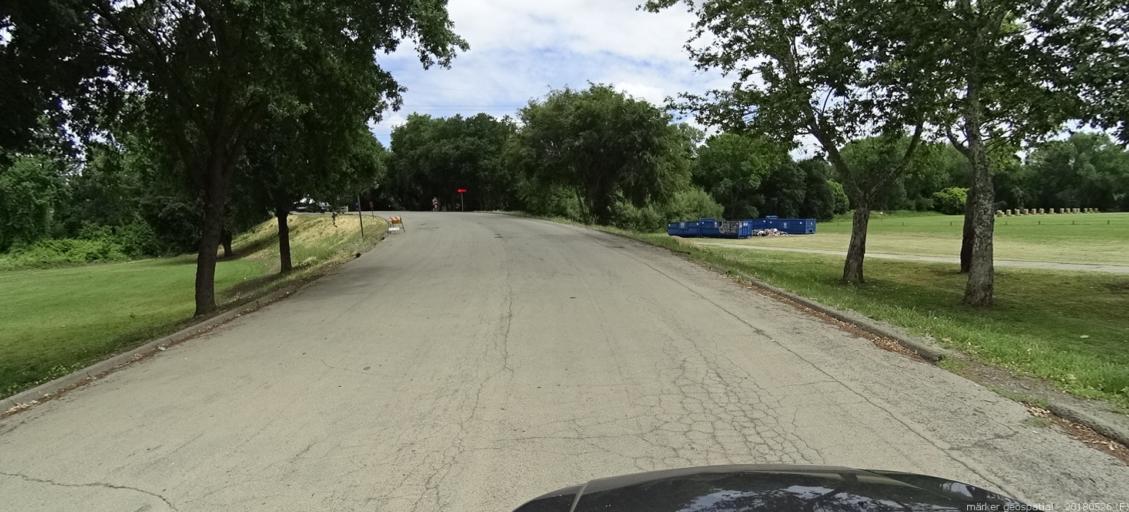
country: US
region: California
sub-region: Sacramento County
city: Sacramento
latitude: 38.6058
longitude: -121.5020
